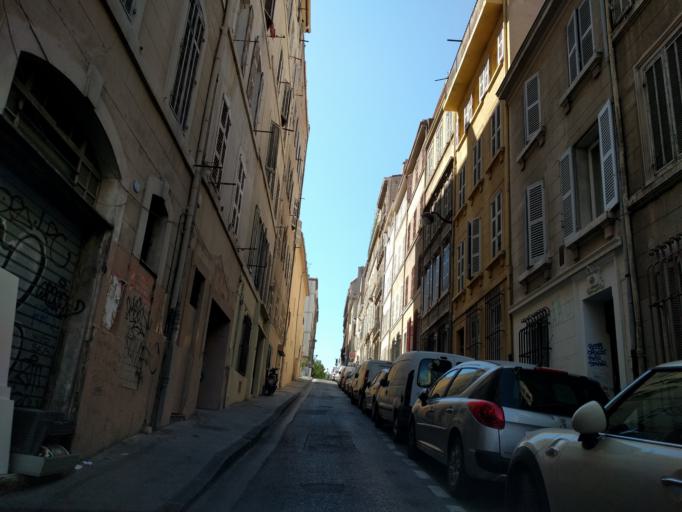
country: FR
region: Provence-Alpes-Cote d'Azur
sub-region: Departement des Bouches-du-Rhone
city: Marseille 01
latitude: 43.2964
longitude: 5.3851
